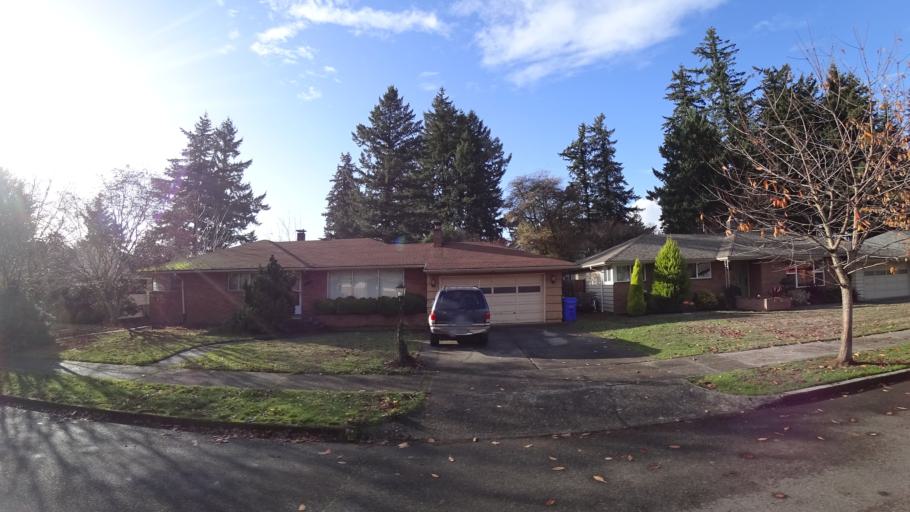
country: US
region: Oregon
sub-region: Multnomah County
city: Lents
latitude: 45.5303
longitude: -122.5524
